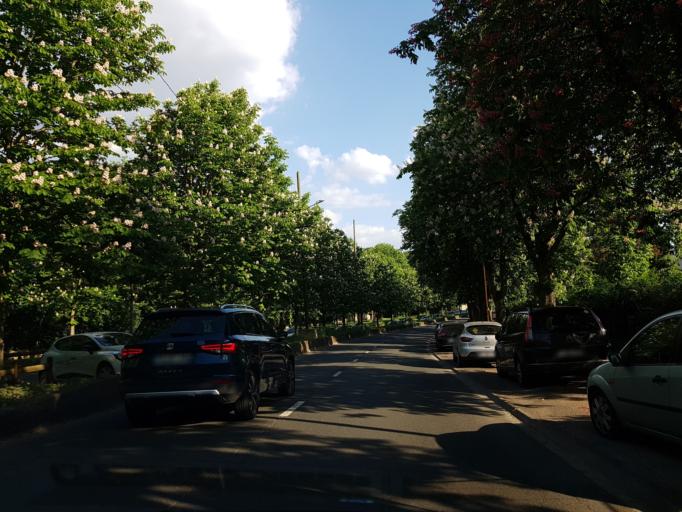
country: FR
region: Ile-de-France
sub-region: Departement des Hauts-de-Seine
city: Sceaux
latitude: 48.7653
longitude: 2.2910
